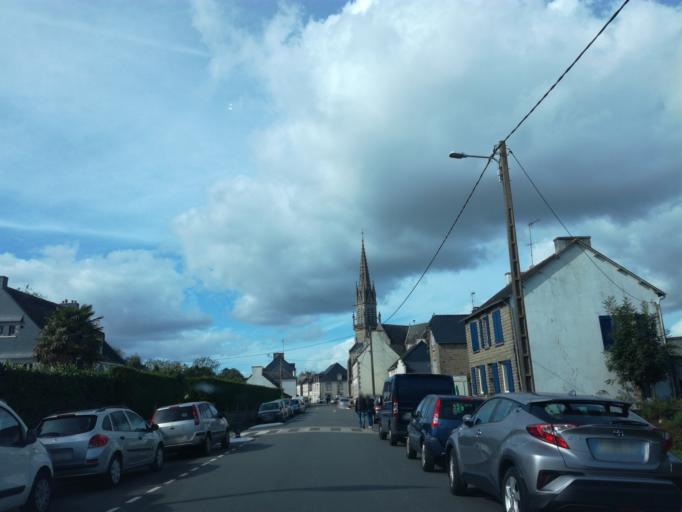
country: FR
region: Brittany
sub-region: Departement du Morbihan
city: Rohan
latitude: 48.0856
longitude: -2.7653
